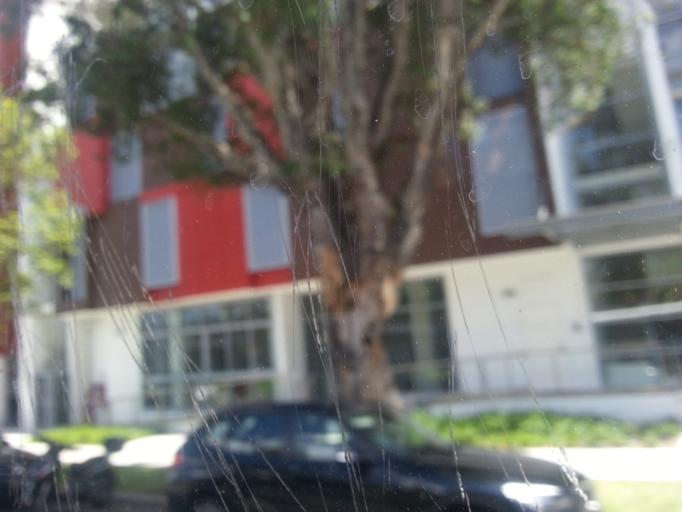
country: AU
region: New South Wales
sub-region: City of Sydney
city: Alexandria
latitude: -33.9026
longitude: 151.1963
